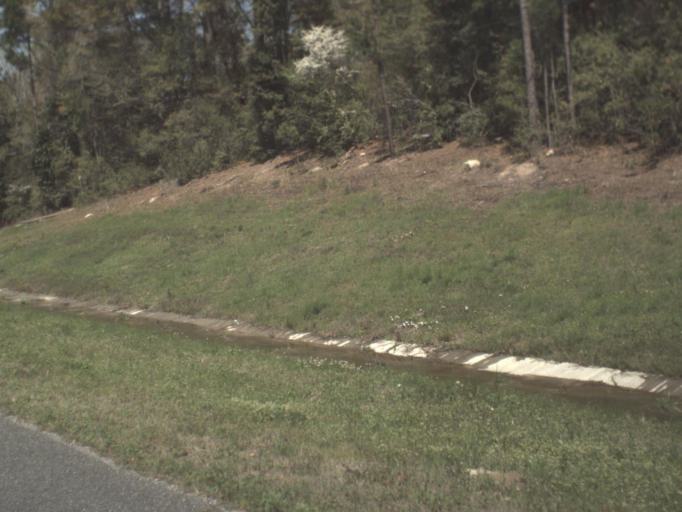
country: US
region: Florida
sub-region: Gadsden County
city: Midway
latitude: 30.5199
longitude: -84.4672
